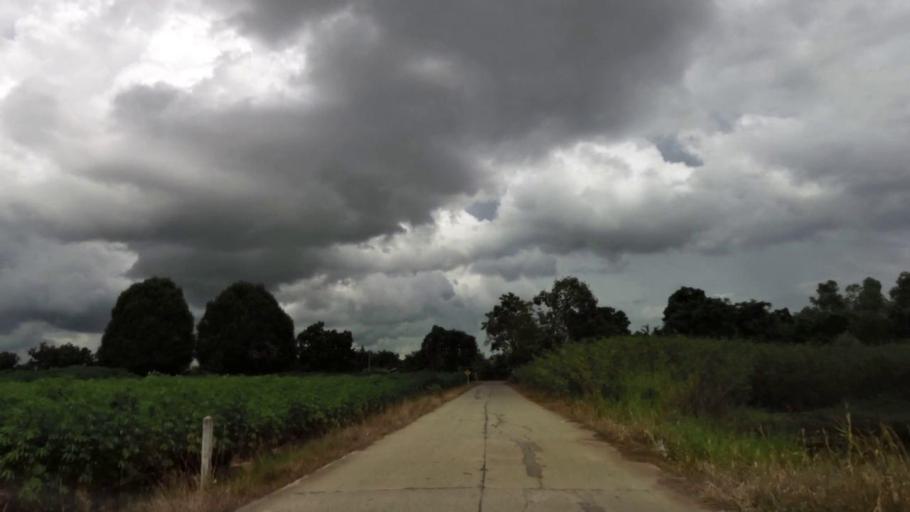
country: TH
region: Nakhon Sawan
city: Phai Sali
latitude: 15.6024
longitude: 100.6571
